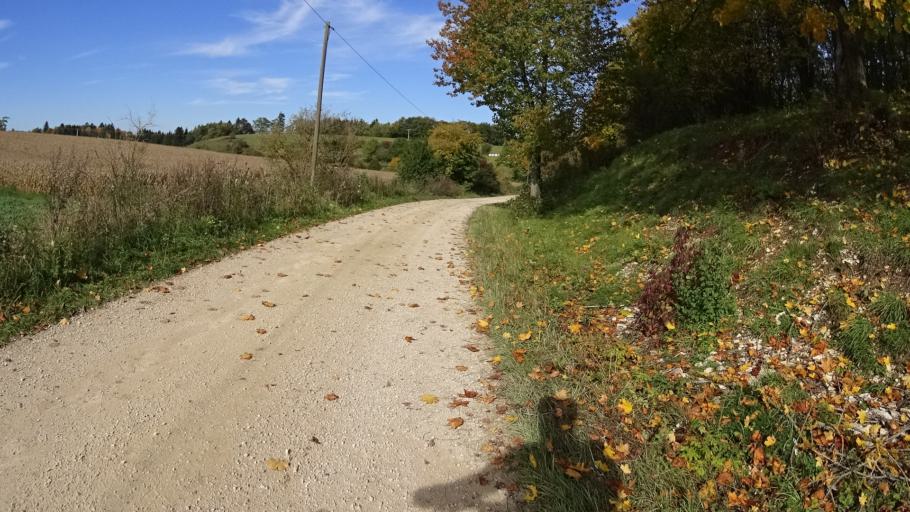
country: DE
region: Bavaria
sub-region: Upper Bavaria
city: Bohmfeld
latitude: 48.8649
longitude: 11.3735
